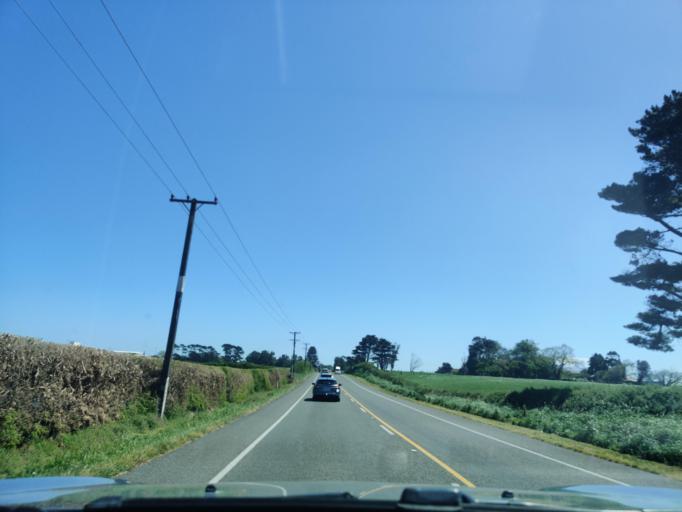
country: NZ
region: Taranaki
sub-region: South Taranaki District
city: Hawera
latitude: -39.6086
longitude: 174.3211
